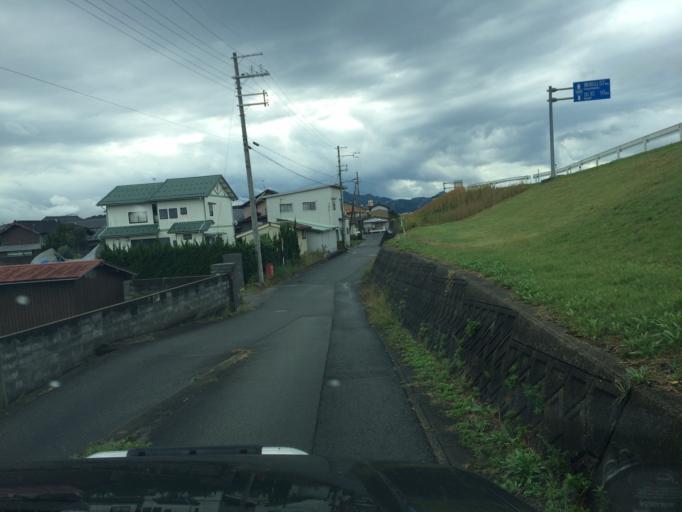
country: JP
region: Hyogo
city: Toyooka
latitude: 35.5250
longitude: 134.8267
